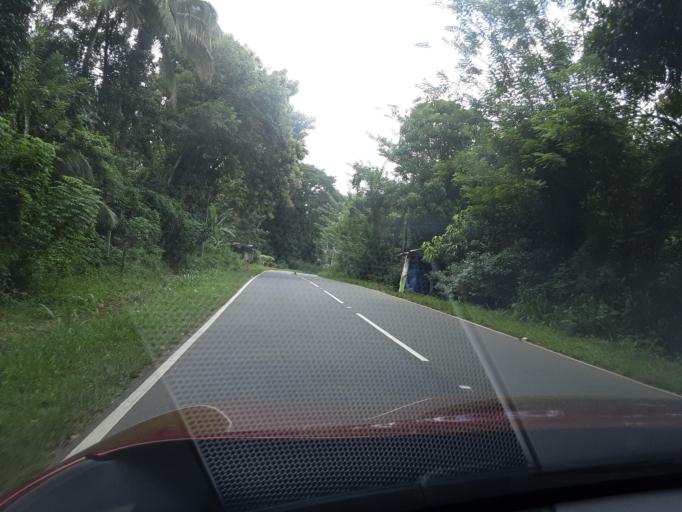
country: LK
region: Uva
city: Monaragala
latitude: 6.8981
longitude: 81.2875
